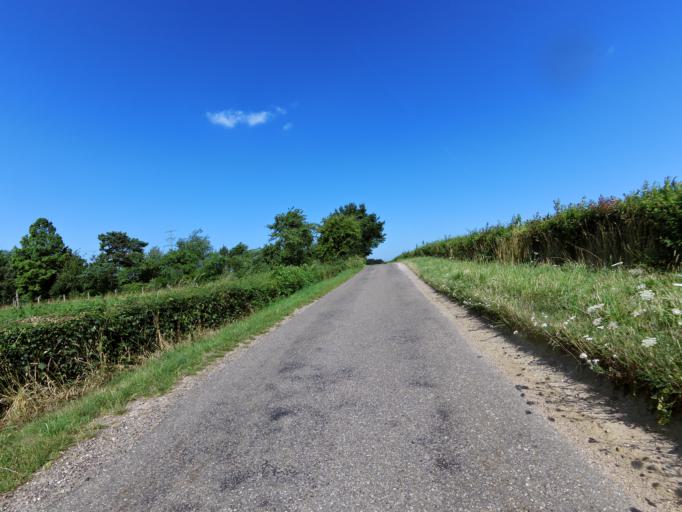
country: NL
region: Limburg
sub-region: Gemeente Voerendaal
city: Klimmen
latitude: 50.8682
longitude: 5.8753
